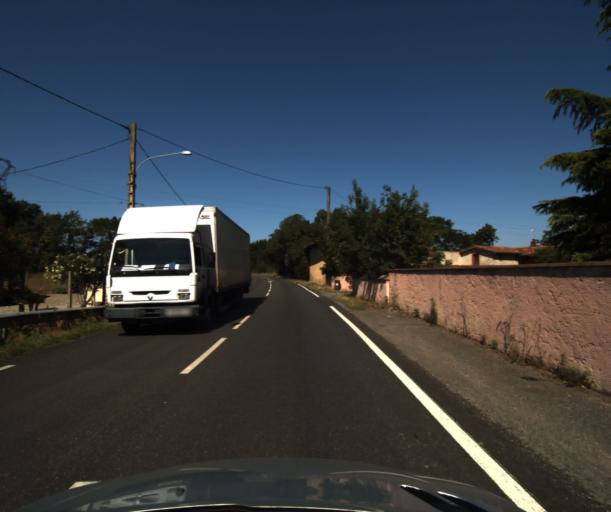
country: FR
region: Midi-Pyrenees
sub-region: Departement de la Haute-Garonne
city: Pinsaguel
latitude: 43.5070
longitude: 1.3804
